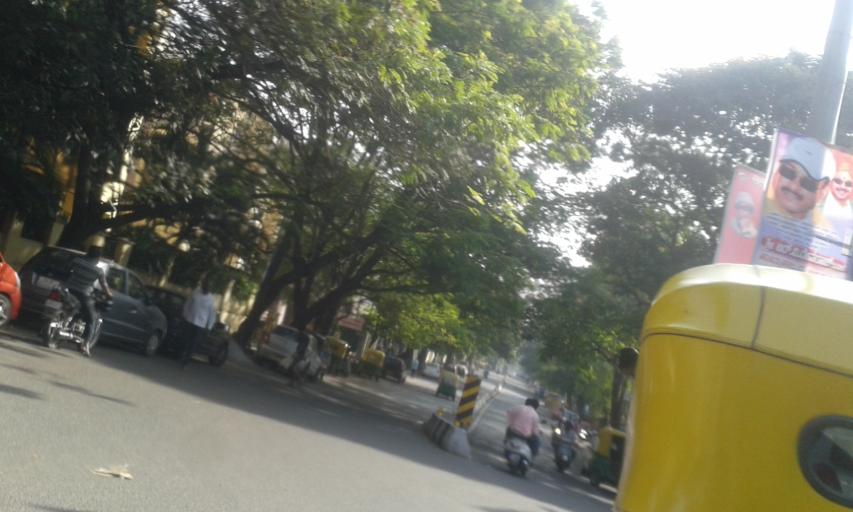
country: IN
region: Karnataka
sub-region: Bangalore Urban
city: Bangalore
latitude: 12.9286
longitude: 77.5894
